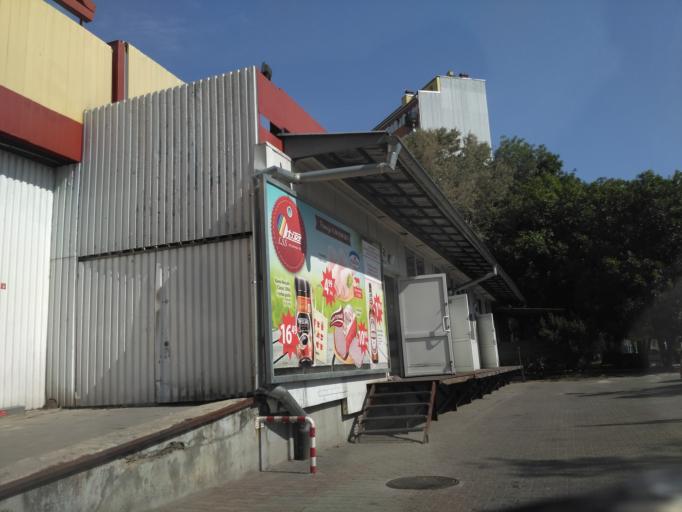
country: PL
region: Lublin Voivodeship
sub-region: Powiat lubelski
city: Lublin
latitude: 51.2114
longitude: 22.5737
